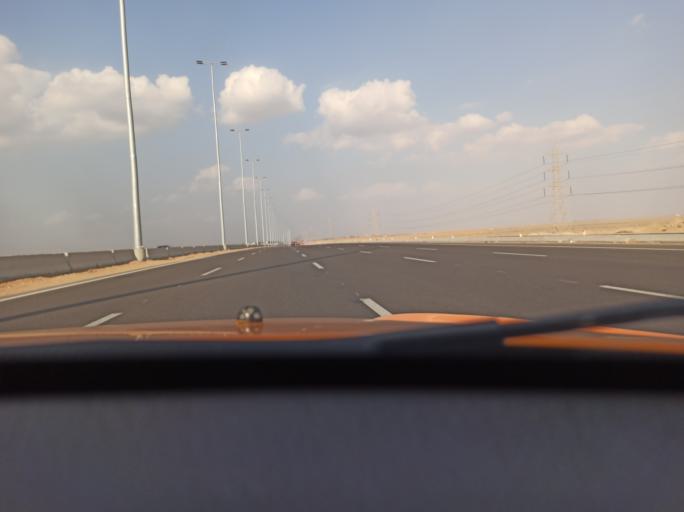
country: EG
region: Al Isma'iliyah
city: At Tall al Kabir
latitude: 30.3717
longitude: 31.9272
